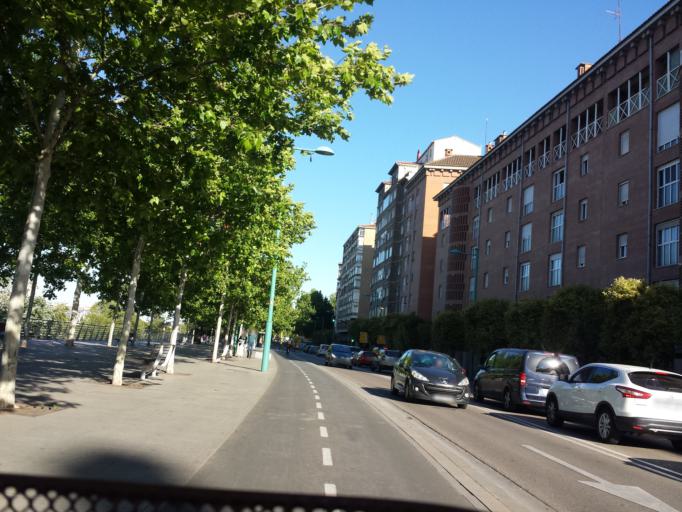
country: ES
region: Aragon
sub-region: Provincia de Zaragoza
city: Zaragoza
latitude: 41.6556
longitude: -0.8748
